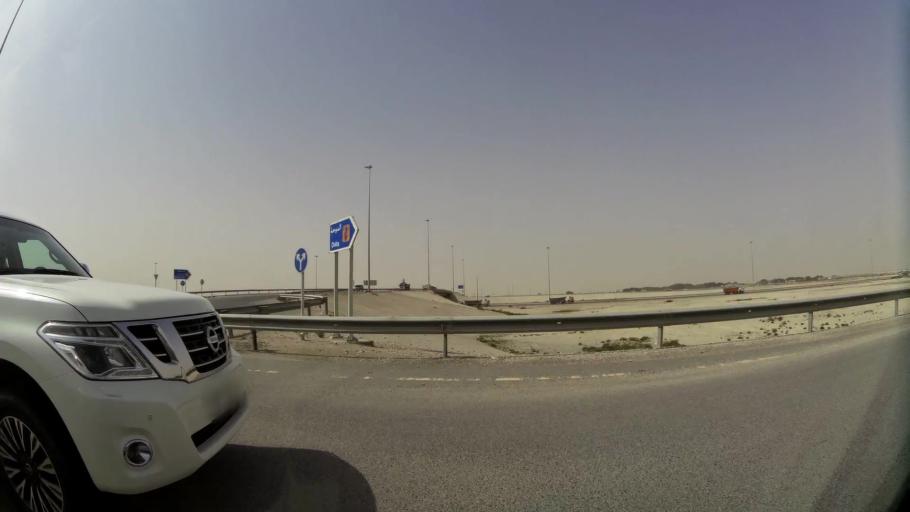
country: QA
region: Baladiyat ar Rayyan
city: Ar Rayyan
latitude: 25.1526
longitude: 51.2787
